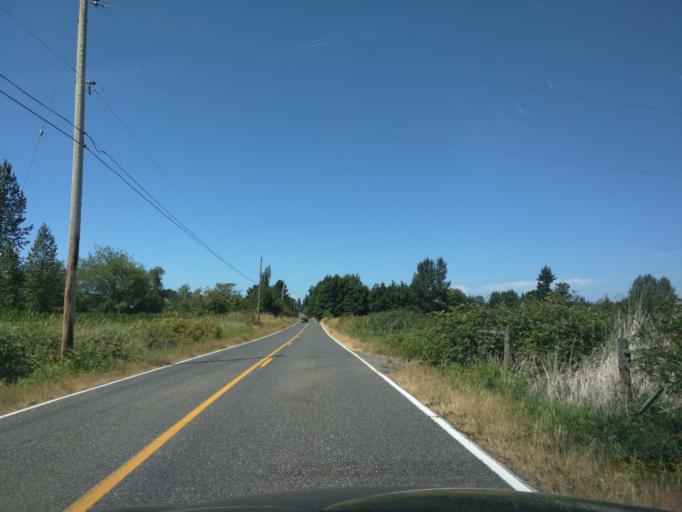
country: US
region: Washington
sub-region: Whatcom County
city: Everson
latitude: 48.8771
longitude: -122.4061
